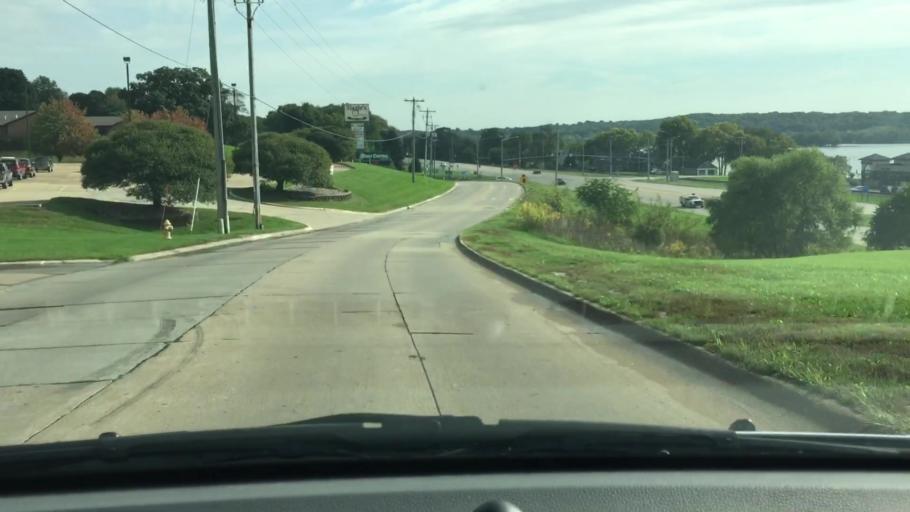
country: US
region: Iowa
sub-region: Scott County
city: Le Claire
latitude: 41.5872
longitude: -90.3606
